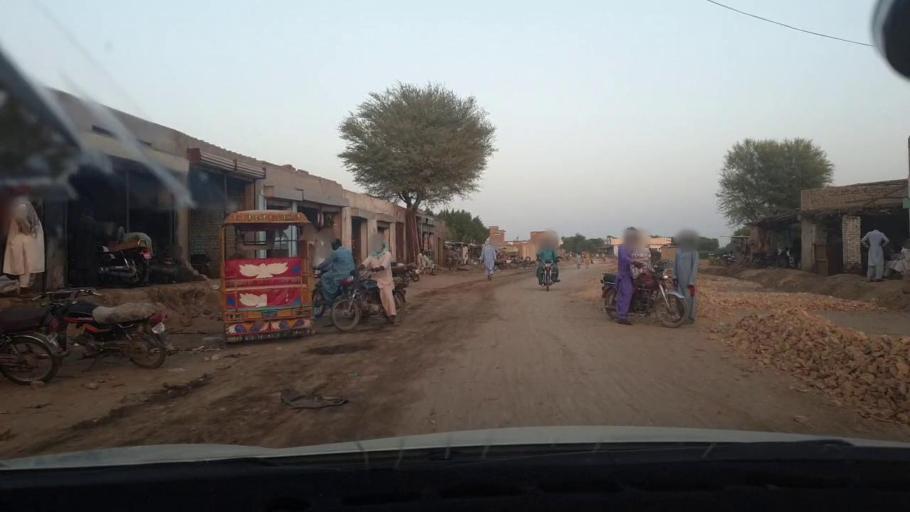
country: PK
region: Sindh
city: Bhit Shah
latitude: 25.7529
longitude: 68.5053
